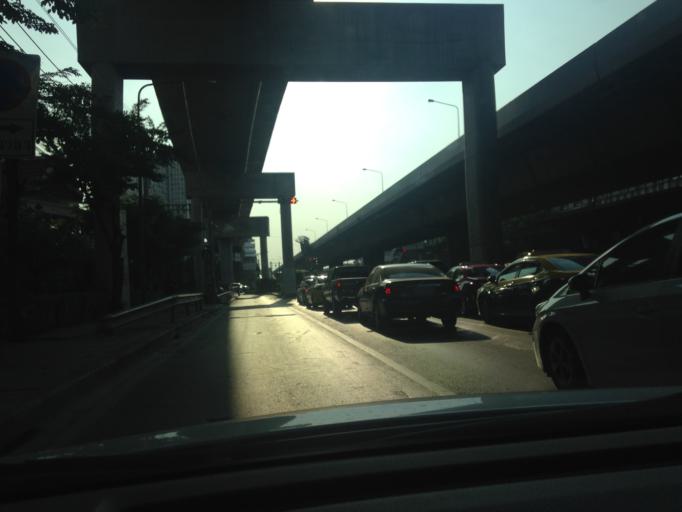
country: TH
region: Bangkok
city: Bangkok Yai
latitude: 13.7157
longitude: 100.4794
